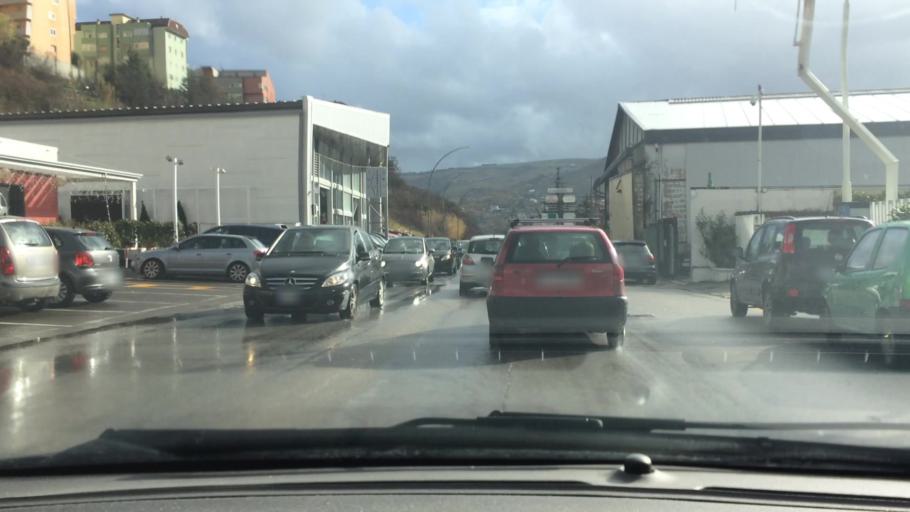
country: IT
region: Basilicate
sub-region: Provincia di Potenza
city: Potenza
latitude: 40.6315
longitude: 15.7897
